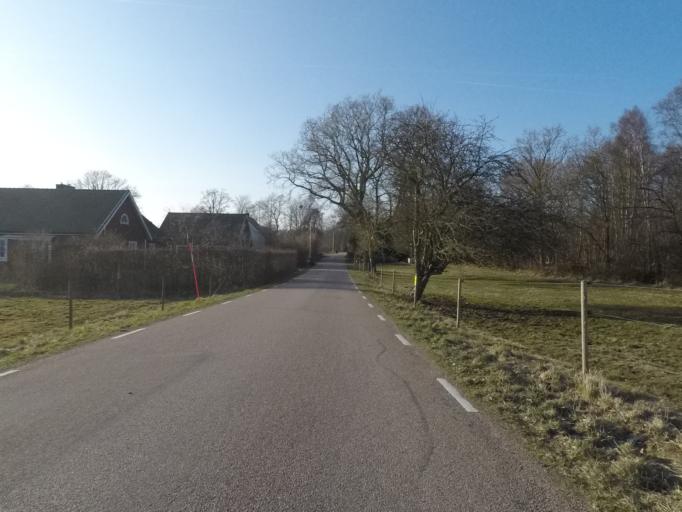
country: SE
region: Skane
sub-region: Hoganas Kommun
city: Hoganas
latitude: 56.2546
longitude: 12.6083
